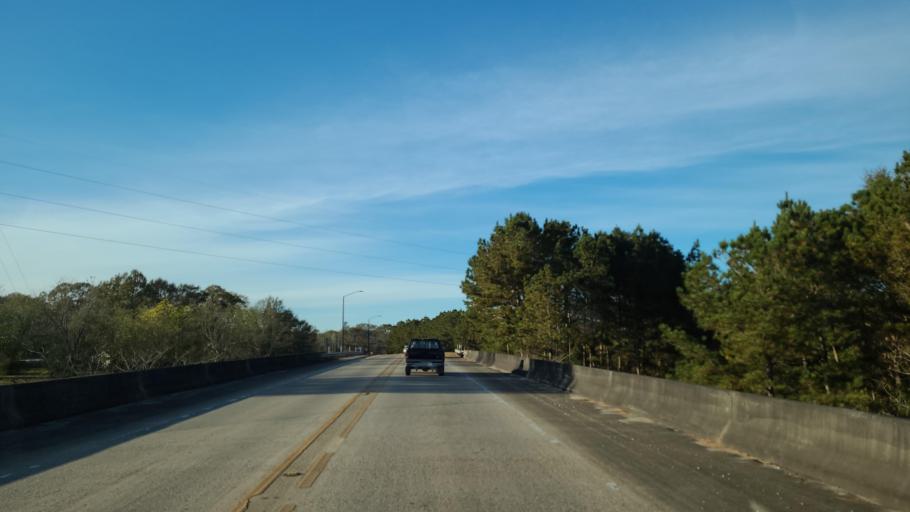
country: US
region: Mississippi
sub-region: Lamar County
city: Purvis
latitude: 31.1497
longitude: -89.4069
